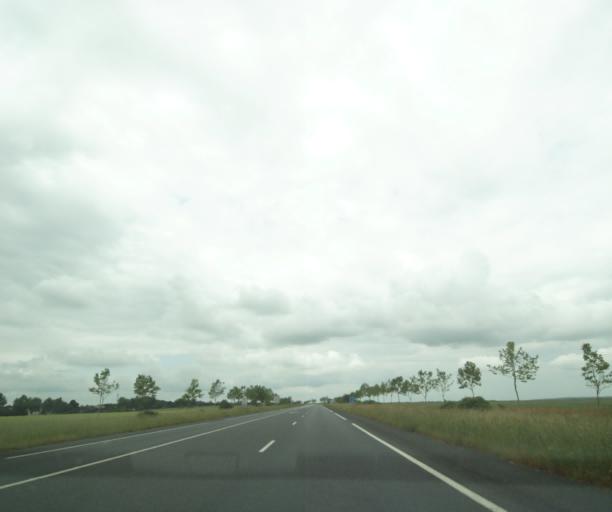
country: FR
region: Poitou-Charentes
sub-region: Departement des Deux-Sevres
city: Saint-Varent
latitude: 46.8980
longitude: -0.1921
